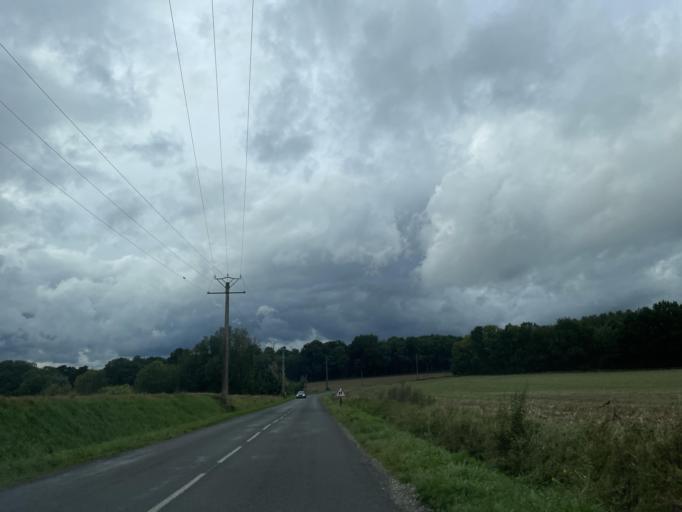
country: FR
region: Ile-de-France
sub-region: Departement de Seine-et-Marne
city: Saint-Jean-les-Deux-Jumeaux
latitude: 48.9331
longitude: 2.9913
